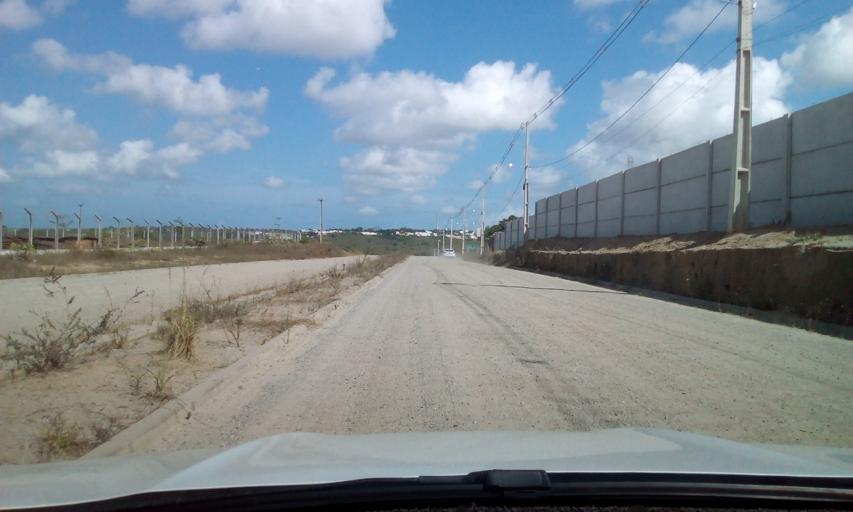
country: BR
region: Paraiba
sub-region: Conde
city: Conde
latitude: -7.2515
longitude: -34.9293
